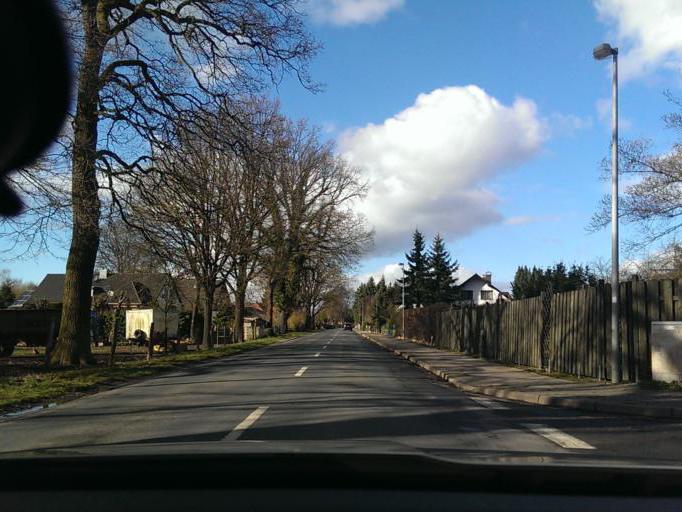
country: DE
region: Lower Saxony
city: Lindwedel
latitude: 52.5511
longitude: 9.6859
